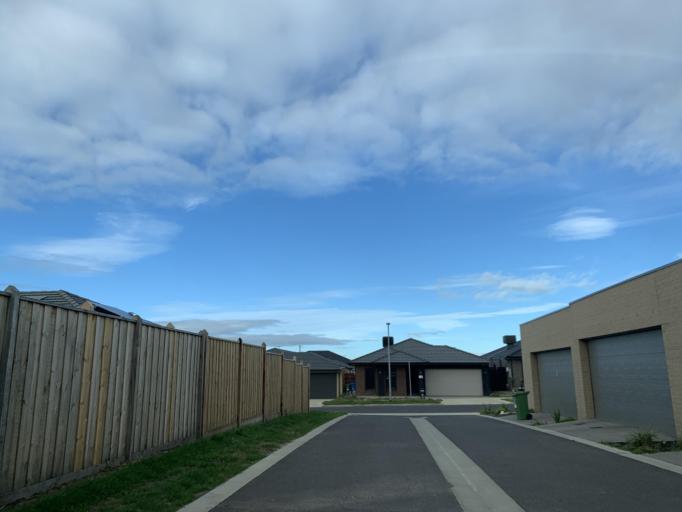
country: AU
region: Victoria
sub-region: Cardinia
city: Officer South
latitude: -38.1231
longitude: 145.3574
